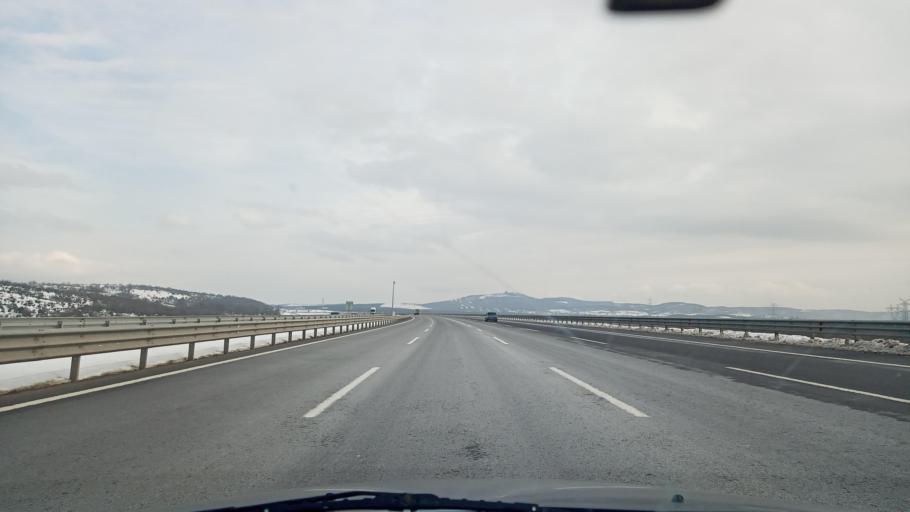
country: TR
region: Kocaeli
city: Mollafeneri
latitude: 40.8884
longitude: 29.5769
